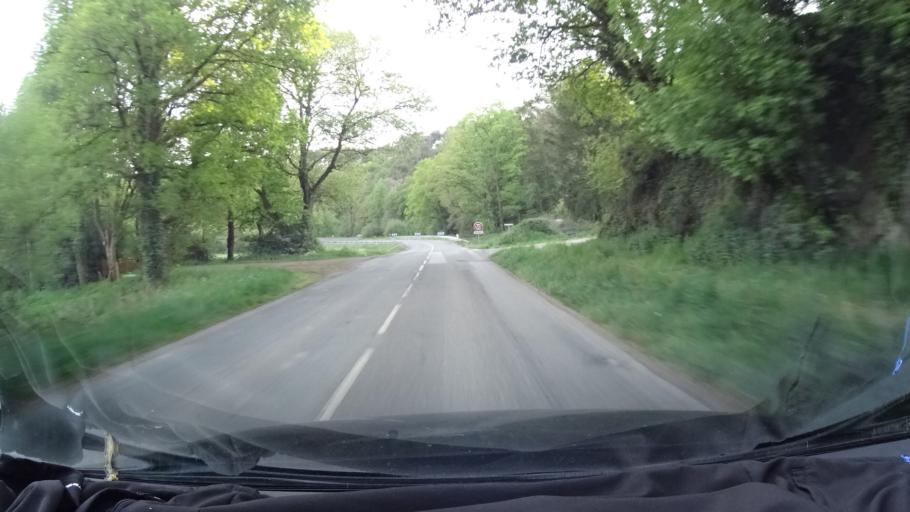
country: FR
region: Brittany
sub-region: Departement du Morbihan
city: Caden
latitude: 47.5923
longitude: -2.2982
